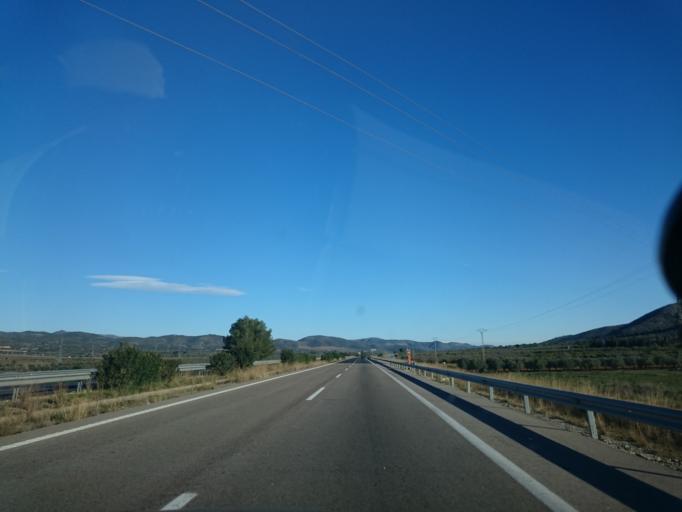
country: ES
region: Valencia
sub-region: Provincia de Castello
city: Alcala de Xivert
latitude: 40.3018
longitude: 0.2368
